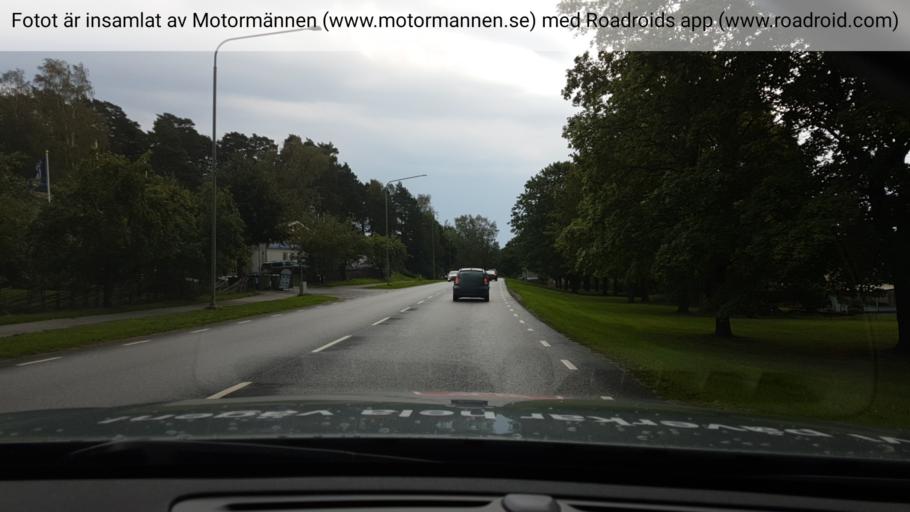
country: SE
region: Uppsala
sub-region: Habo Kommun
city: Balsta
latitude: 59.5634
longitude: 17.5378
